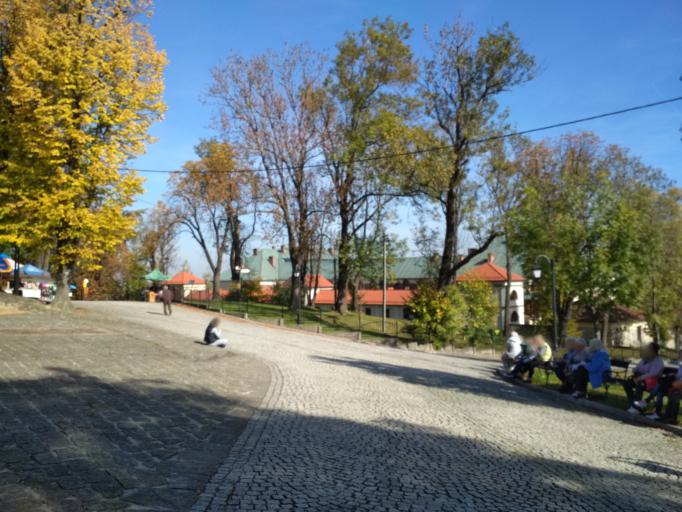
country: PL
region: Lesser Poland Voivodeship
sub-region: Powiat wadowicki
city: Kalwaria Zebrzydowska
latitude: 49.8602
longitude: 19.6734
